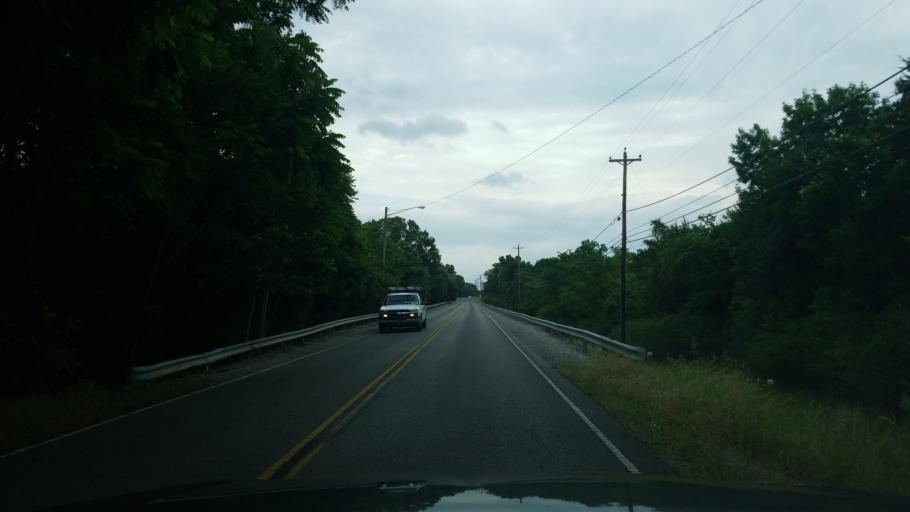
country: US
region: Tennessee
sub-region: Rutherford County
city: La Vergne
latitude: 36.0813
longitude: -86.5926
